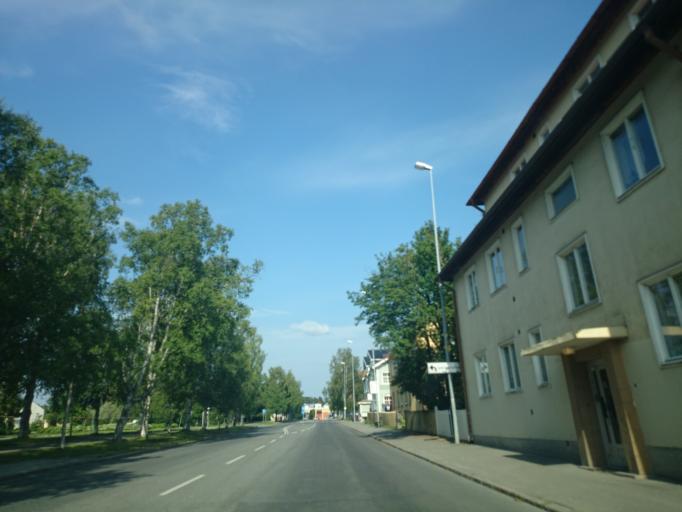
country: SE
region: Jaemtland
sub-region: OEstersunds Kommun
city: Ostersund
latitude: 63.1742
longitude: 14.6508
